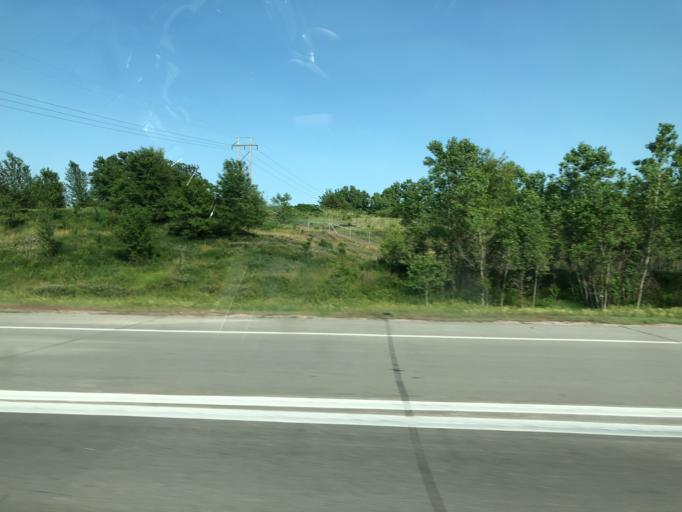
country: US
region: Nebraska
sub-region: Saunders County
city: Ashland
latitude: 41.0167
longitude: -96.3047
